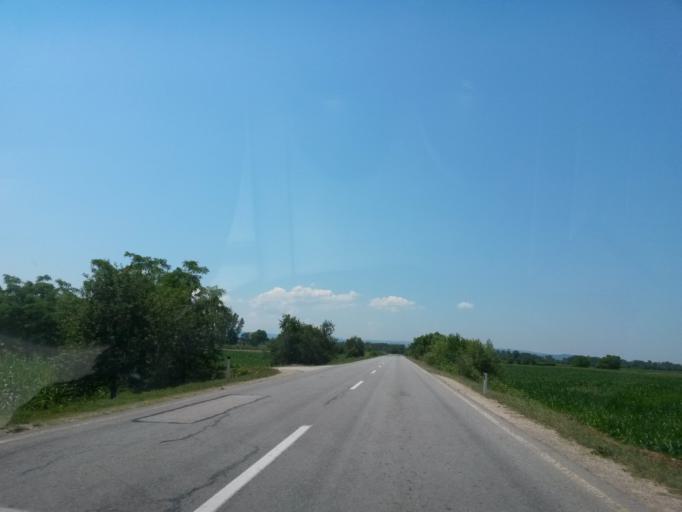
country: BA
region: Federation of Bosnia and Herzegovina
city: Odzak
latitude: 45.0035
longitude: 18.3901
